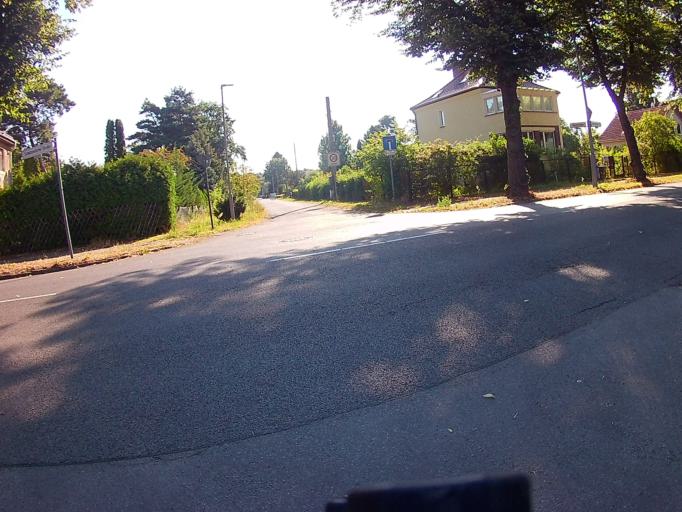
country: DE
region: Berlin
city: Bohnsdorf
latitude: 52.3957
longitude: 13.5842
